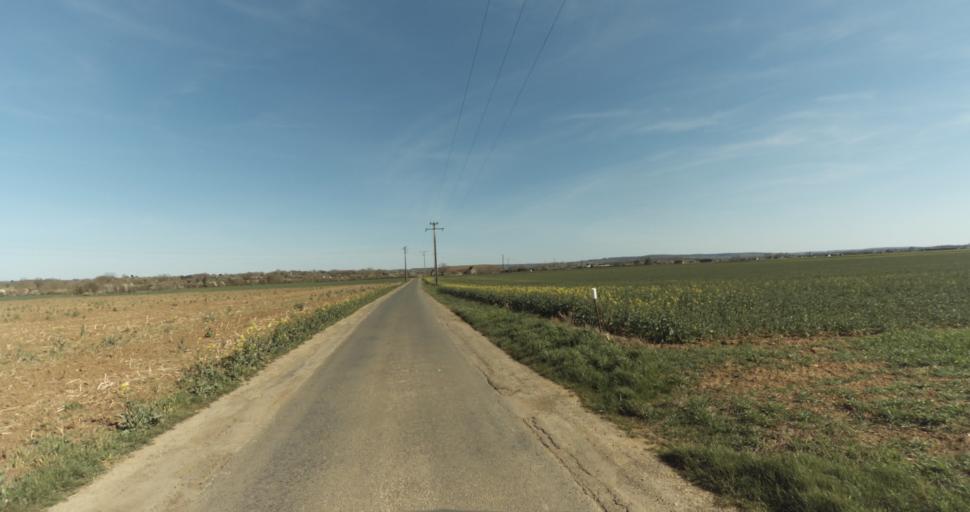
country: FR
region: Lower Normandy
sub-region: Departement du Calvados
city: Saint-Pierre-sur-Dives
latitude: 49.0512
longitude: -0.0434
